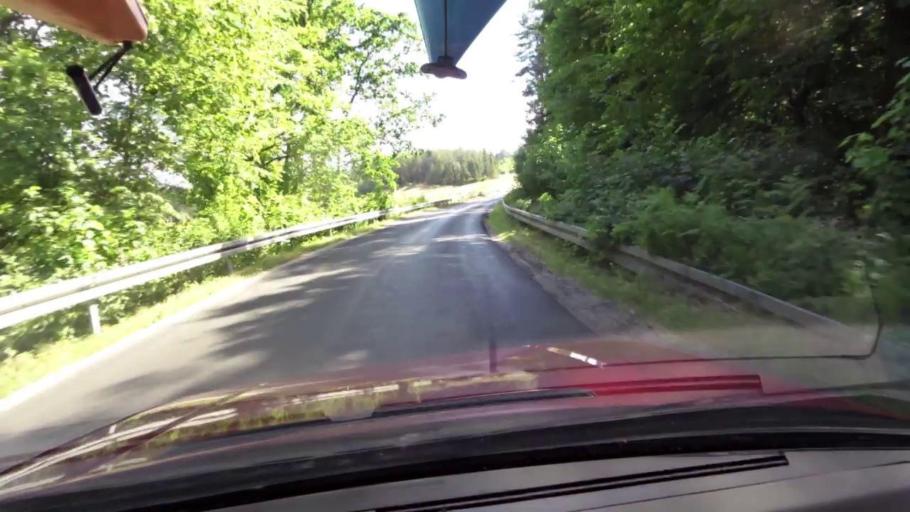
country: PL
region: Pomeranian Voivodeship
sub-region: Powiat slupski
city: Kepice
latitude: 54.2104
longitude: 16.8945
